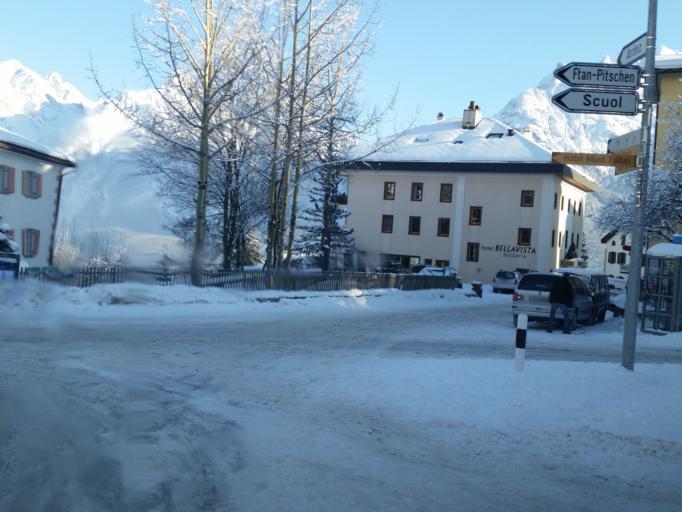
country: CH
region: Grisons
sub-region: Inn District
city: Scuol
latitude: 46.7929
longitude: 10.2472
